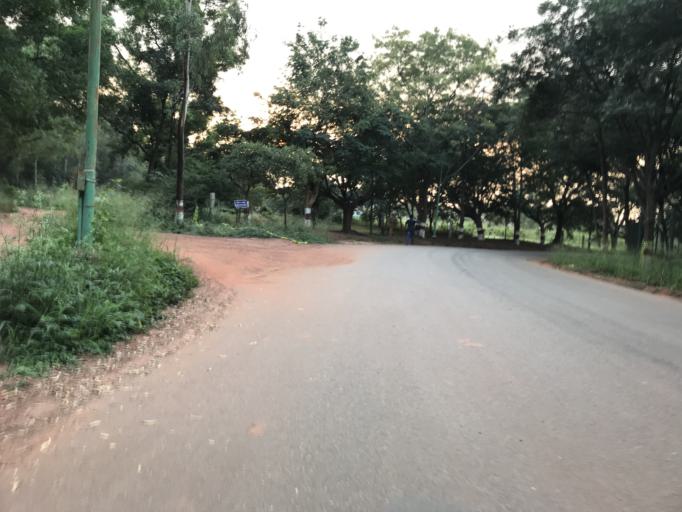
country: IN
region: Karnataka
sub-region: Bangalore Urban
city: Yelahanka
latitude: 13.0775
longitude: 77.5765
